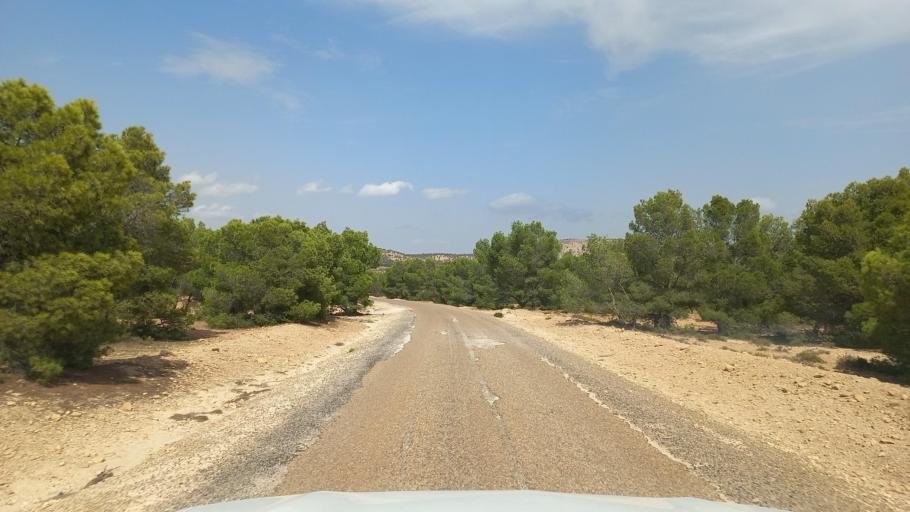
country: TN
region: Al Qasrayn
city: Sbiba
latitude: 35.4011
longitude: 8.9195
